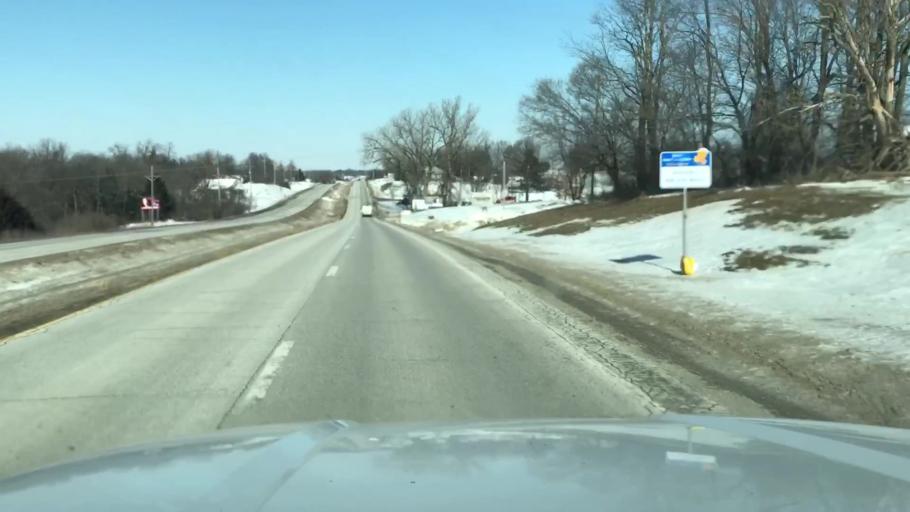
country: US
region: Missouri
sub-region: Andrew County
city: Savannah
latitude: 39.9133
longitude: -94.8103
